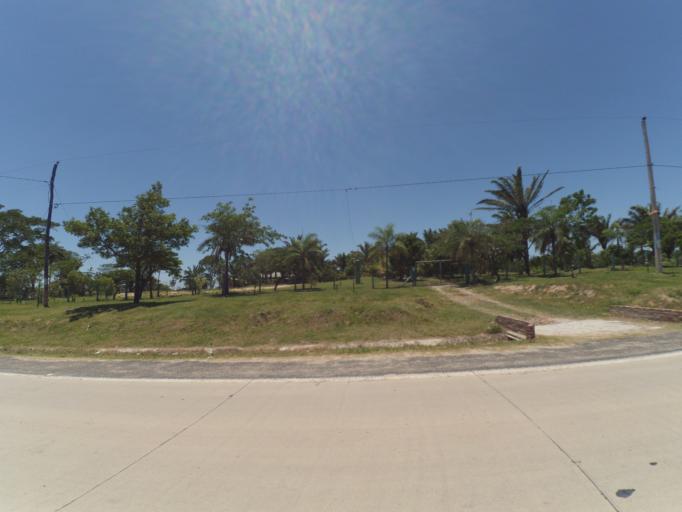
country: BO
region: Santa Cruz
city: Santa Cruz de la Sierra
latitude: -17.8185
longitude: -63.2854
